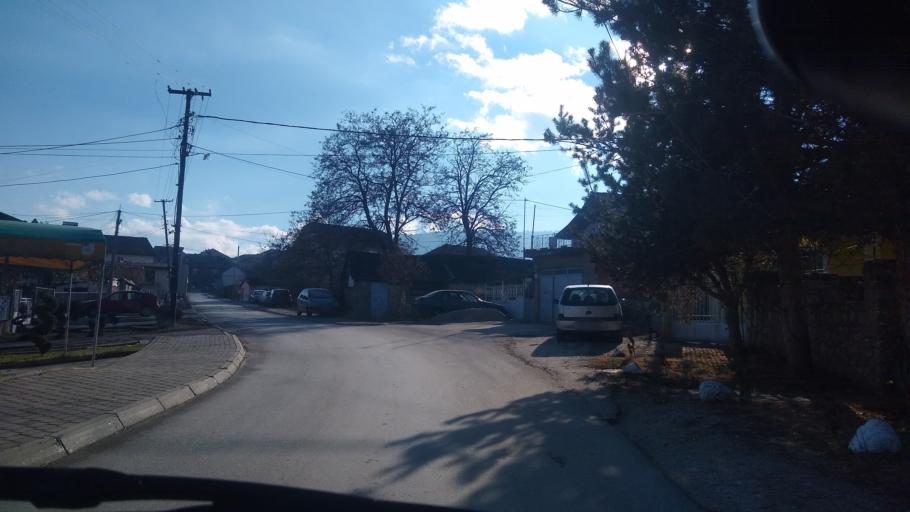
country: MK
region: Bitola
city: Bitola
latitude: 41.0095
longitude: 21.3455
